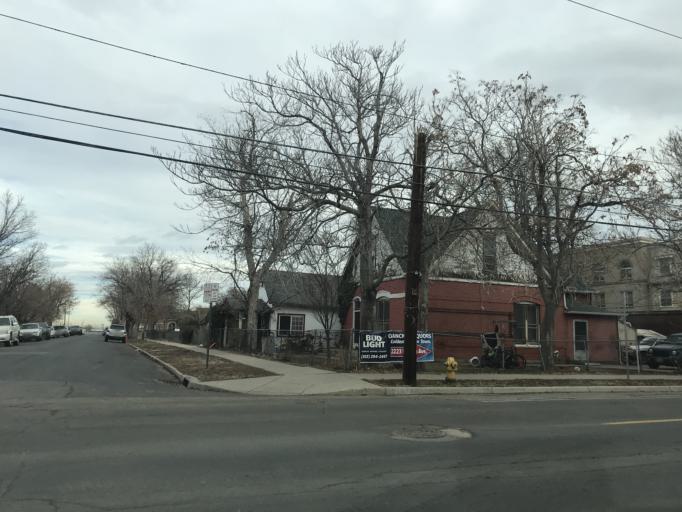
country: US
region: Colorado
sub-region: Adams County
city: Commerce City
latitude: 39.7819
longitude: -104.9656
